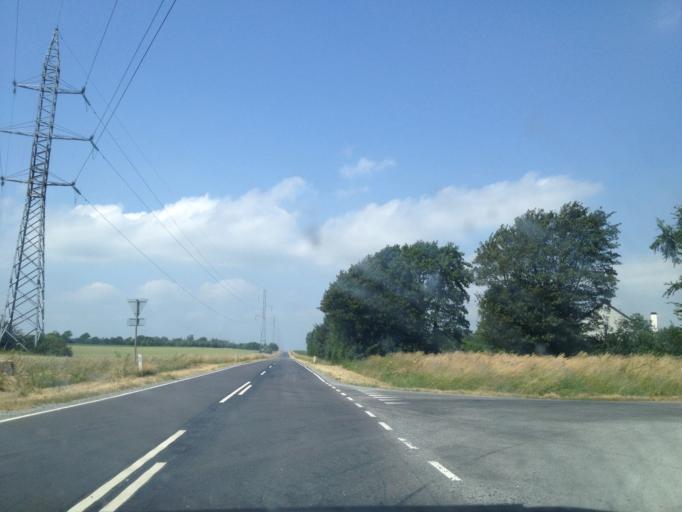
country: DK
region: South Denmark
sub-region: Haderslev Kommune
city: Vojens
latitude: 55.3363
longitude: 9.2990
